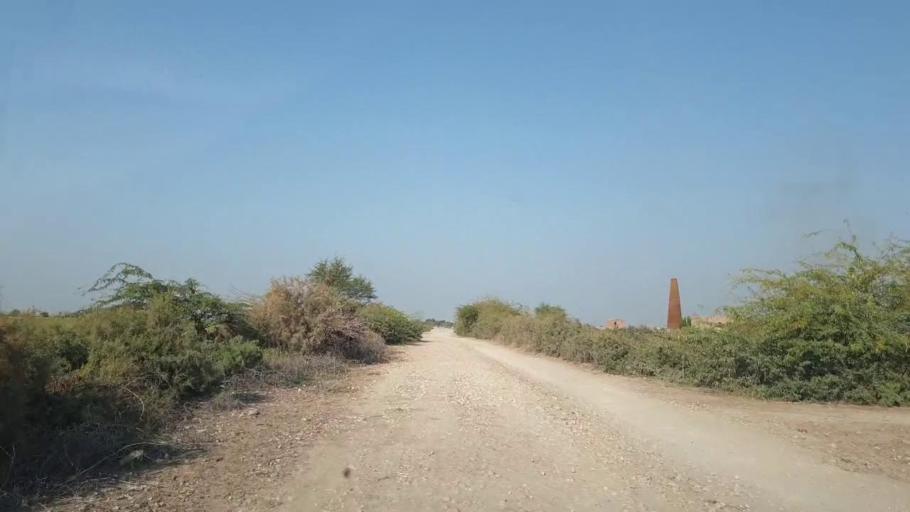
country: PK
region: Sindh
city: Tando Mittha Khan
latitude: 25.7386
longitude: 69.1917
